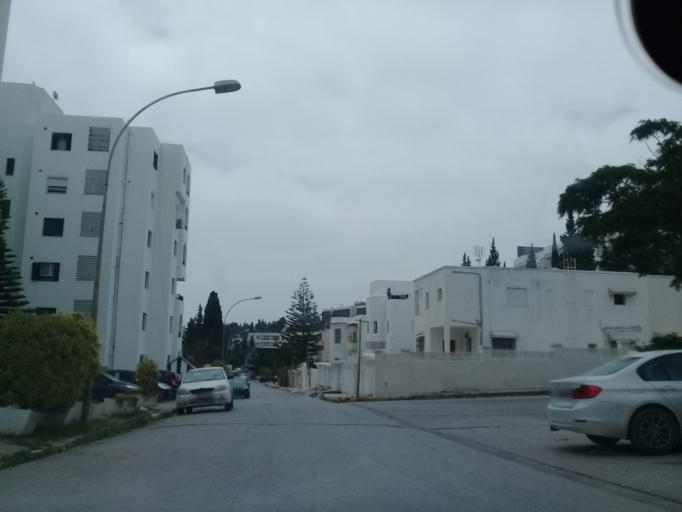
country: TN
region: Tunis
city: Tunis
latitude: 36.8362
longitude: 10.1559
